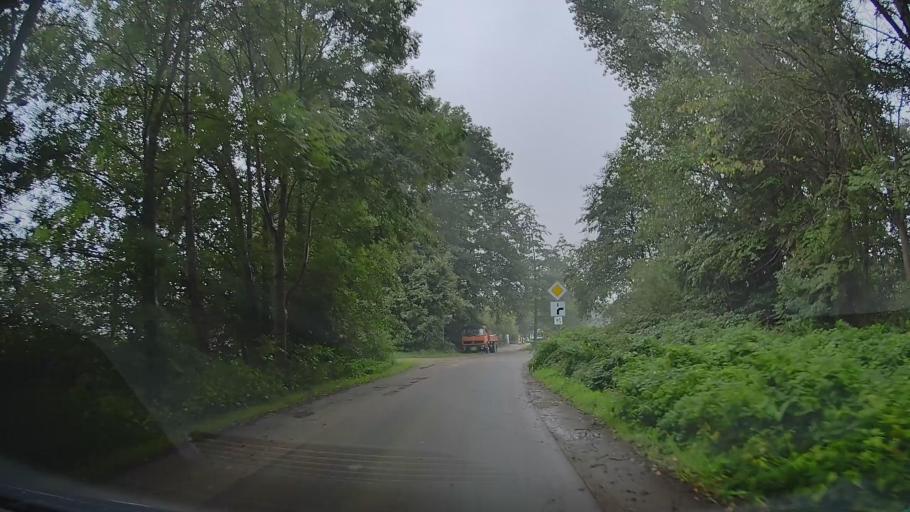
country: DE
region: Mecklenburg-Vorpommern
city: Gramkow
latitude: 53.9281
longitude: 11.3609
